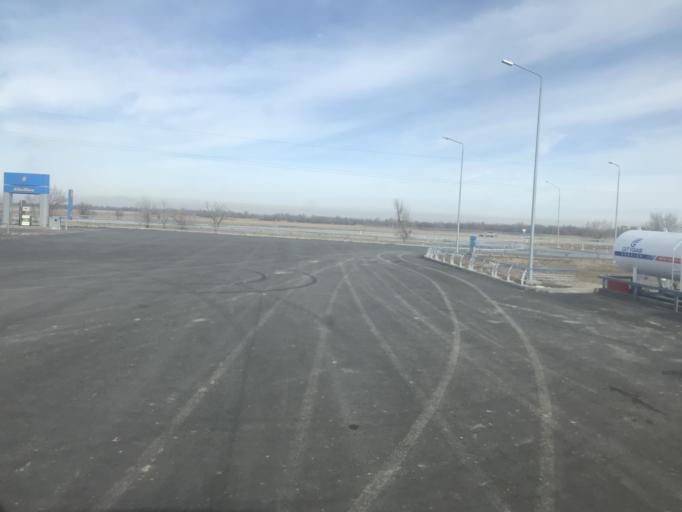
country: KZ
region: Zhambyl
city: Sarykemer
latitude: 43.0083
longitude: 71.7853
